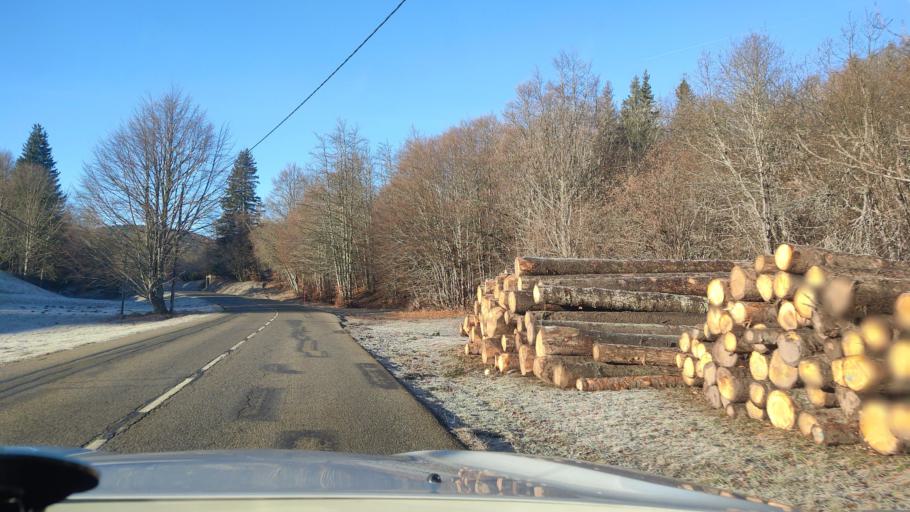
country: FR
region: Rhone-Alpes
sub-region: Departement de la Savoie
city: Mery
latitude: 45.6464
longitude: 6.0041
